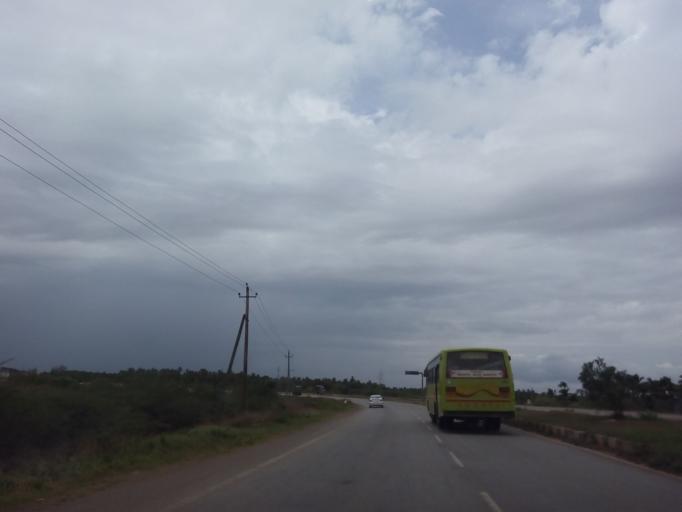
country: IN
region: Karnataka
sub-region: Davanagere
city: Harihar
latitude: 14.4902
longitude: 75.7820
